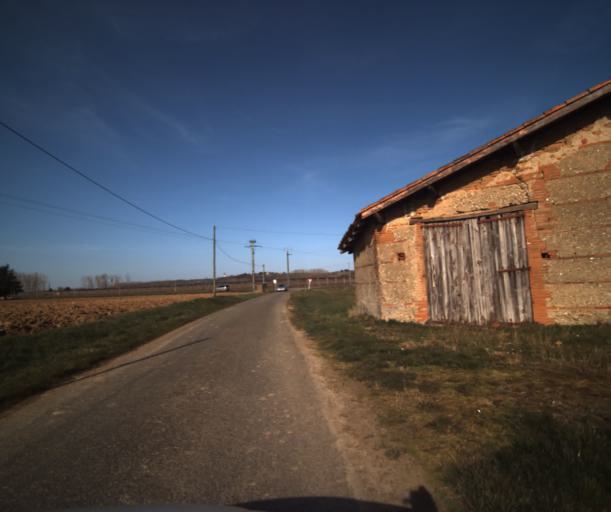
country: FR
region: Midi-Pyrenees
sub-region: Departement du Tarn-et-Garonne
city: Corbarieu
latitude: 43.9354
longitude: 1.3592
